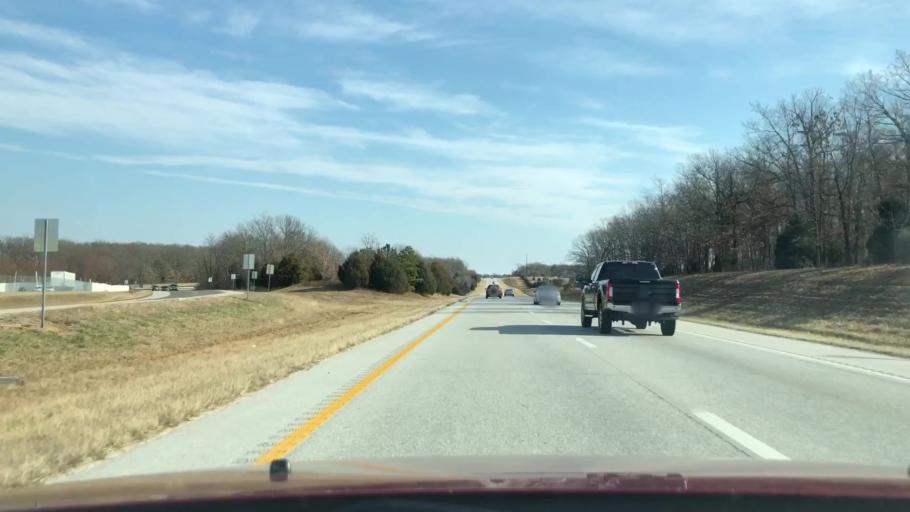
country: US
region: Missouri
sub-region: Webster County
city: Rogersville
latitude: 37.1189
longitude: -93.0134
